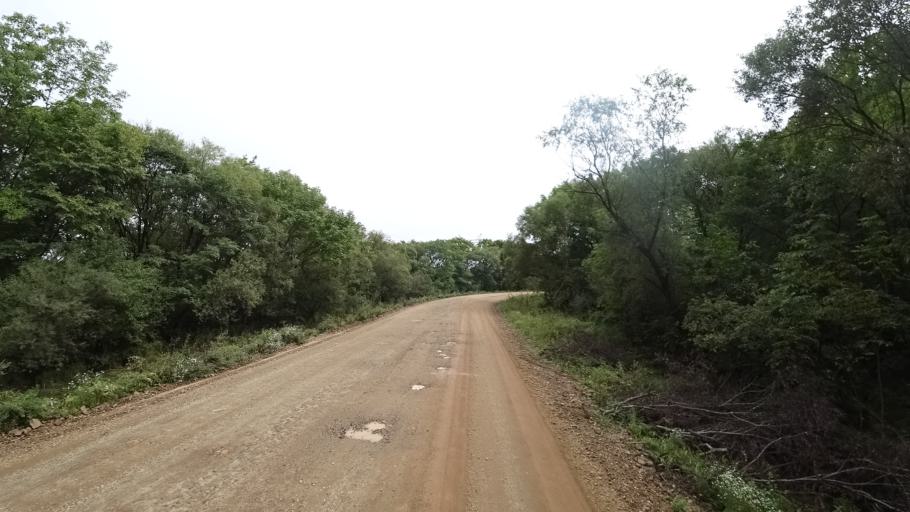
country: RU
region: Primorskiy
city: Lyalichi
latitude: 44.0812
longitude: 132.4502
